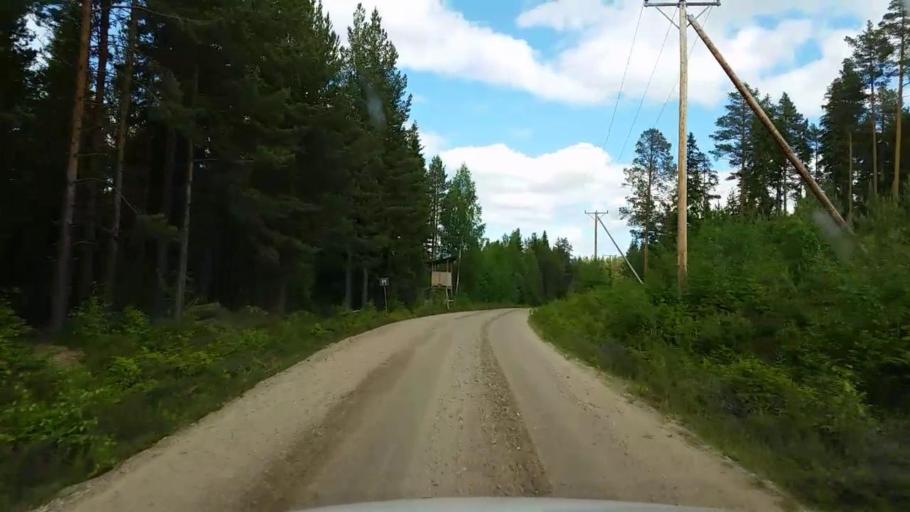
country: SE
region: Gaevleborg
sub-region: Ovanakers Kommun
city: Edsbyn
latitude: 61.5285
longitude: 15.9456
